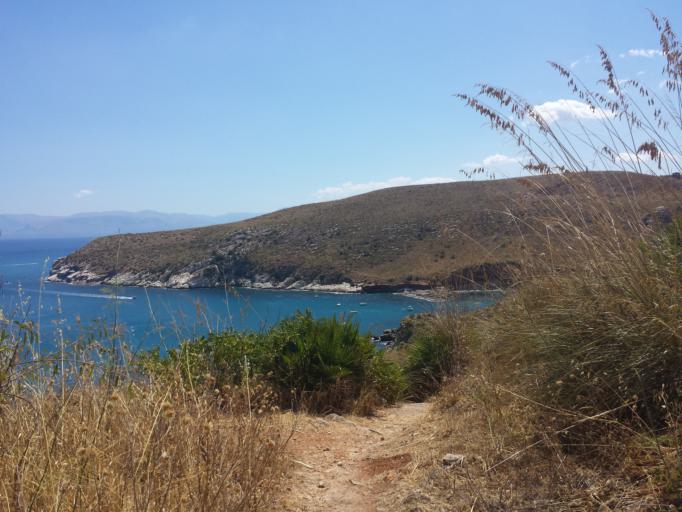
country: IT
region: Sicily
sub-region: Trapani
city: Castellammare del Golfo
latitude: 38.0493
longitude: 12.8537
